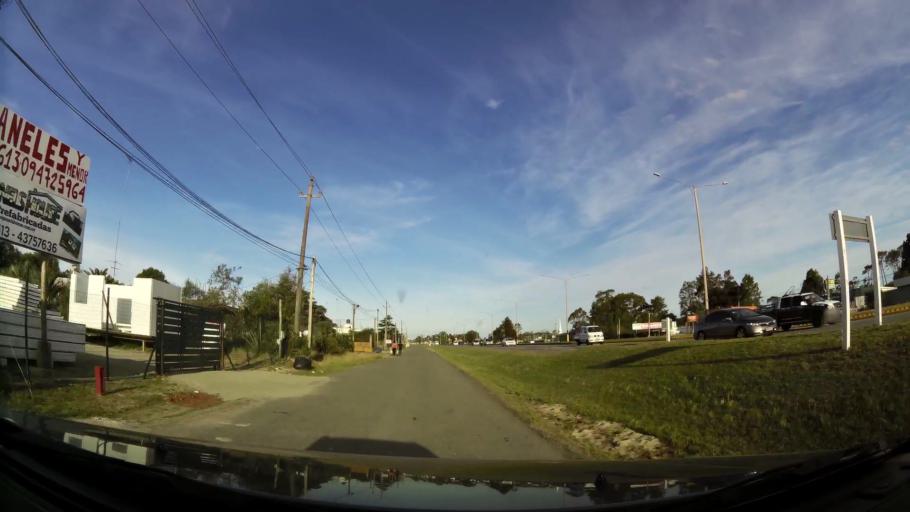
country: UY
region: Canelones
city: Empalme Olmos
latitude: -34.7773
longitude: -55.8548
